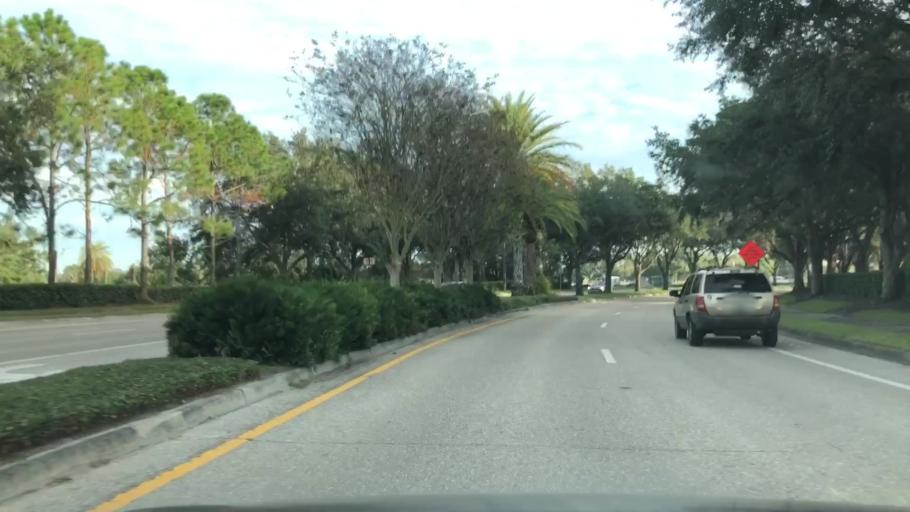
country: US
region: Florida
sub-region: Sarasota County
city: Fruitville
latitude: 27.3414
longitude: -82.4525
